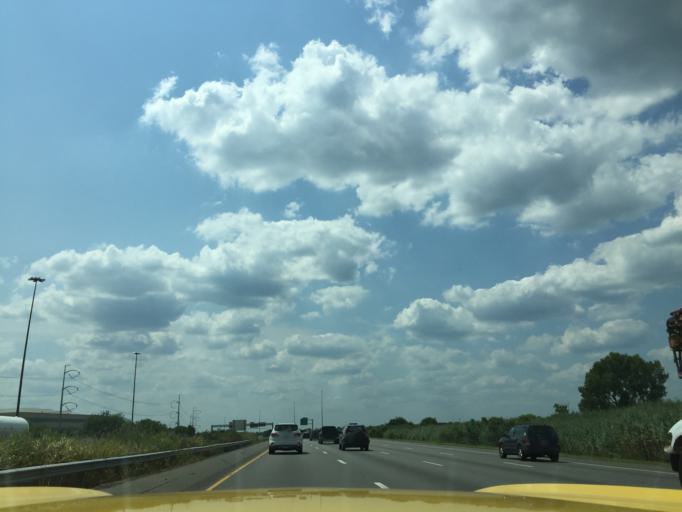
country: US
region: Pennsylvania
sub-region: Delaware County
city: Folcroft
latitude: 39.8760
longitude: -75.2752
